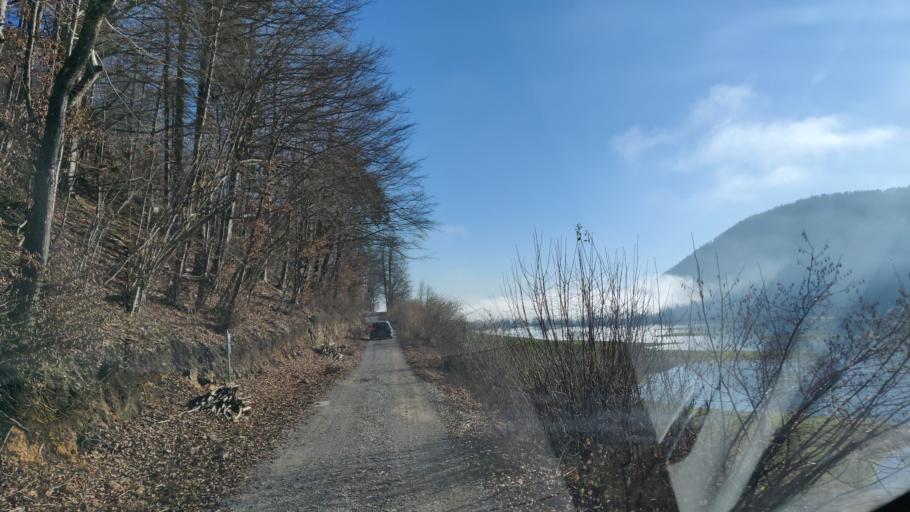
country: SI
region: Logatec
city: Logatec
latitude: 45.8699
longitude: 14.2222
